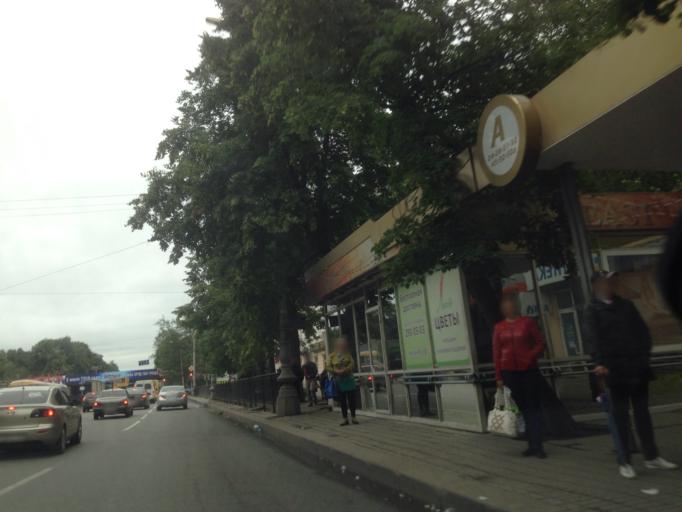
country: RU
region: Sverdlovsk
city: Yekaterinburg
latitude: 56.8411
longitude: 60.6302
